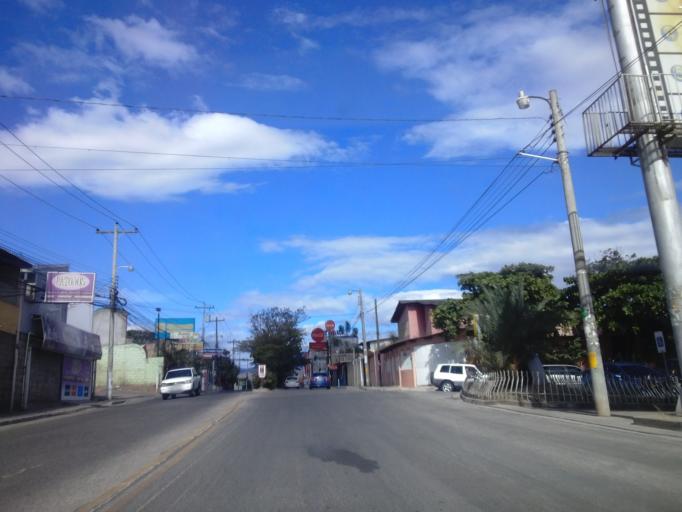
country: HN
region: Francisco Morazan
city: Tegucigalpa
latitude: 14.0532
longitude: -87.2244
